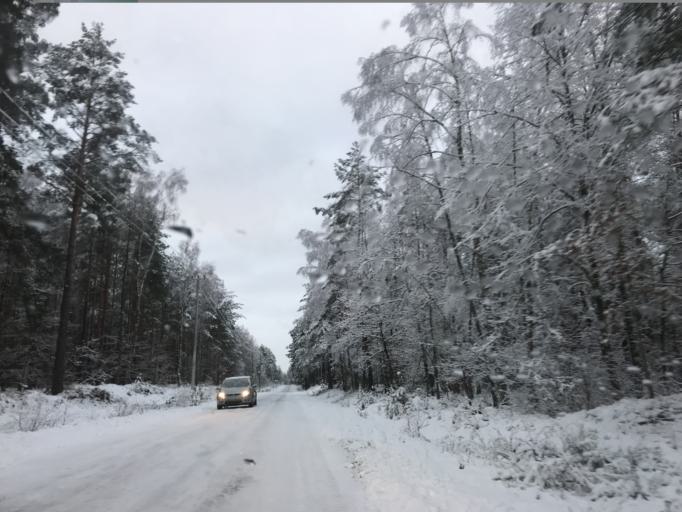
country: PL
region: Pomeranian Voivodeship
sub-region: Powiat bytowski
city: Czarna Dabrowka
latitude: 54.2845
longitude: 17.5981
